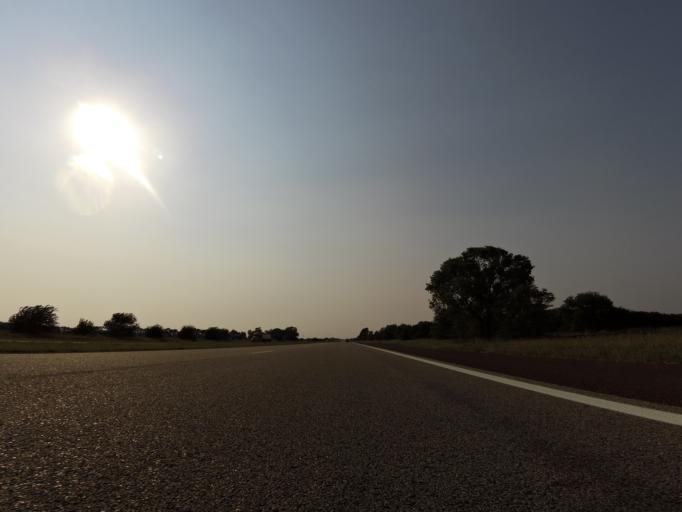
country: US
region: Kansas
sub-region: Reno County
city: Haven
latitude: 37.9184
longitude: -97.8247
